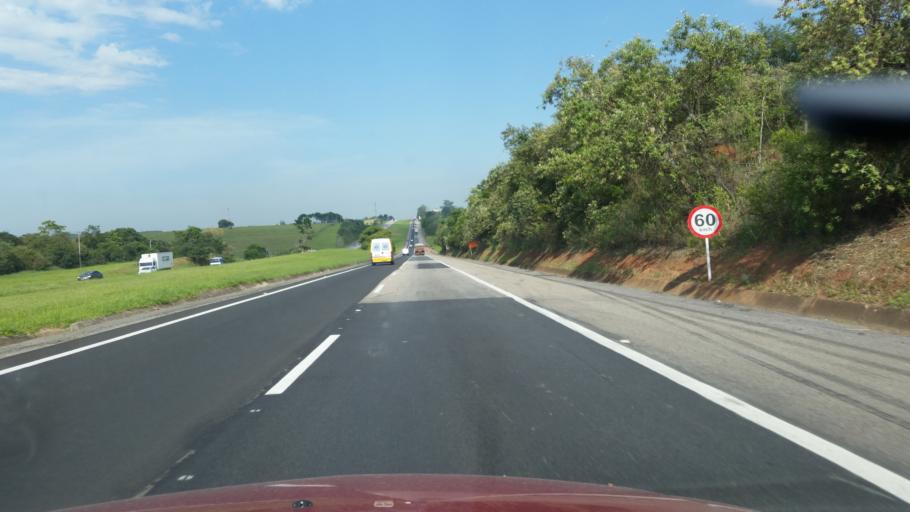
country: BR
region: Sao Paulo
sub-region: Sorocaba
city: Sorocaba
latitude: -23.3784
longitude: -47.4077
